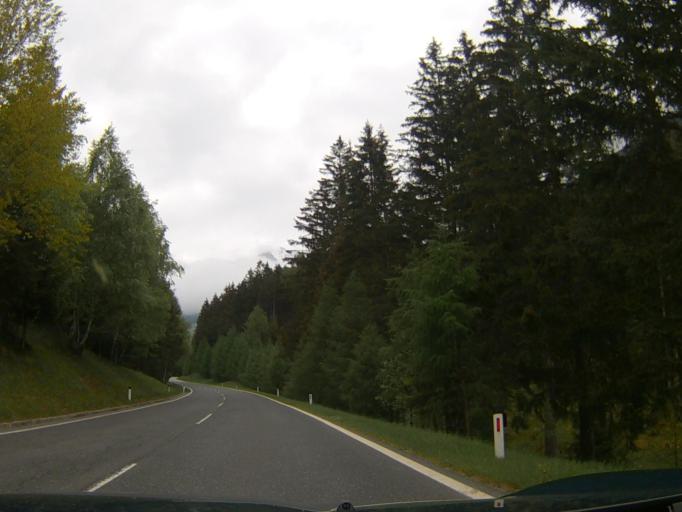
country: AT
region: Carinthia
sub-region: Politischer Bezirk Spittal an der Drau
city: Obervellach
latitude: 46.9502
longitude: 13.1824
